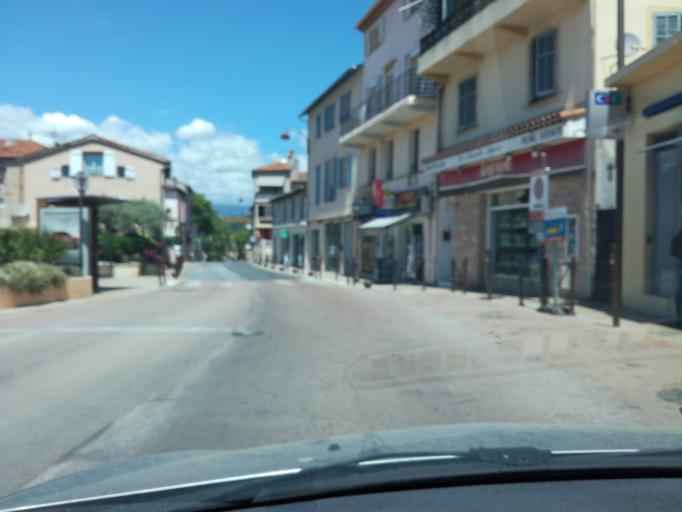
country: FR
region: Provence-Alpes-Cote d'Azur
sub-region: Departement des Alpes-Maritimes
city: Mougins
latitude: 43.5984
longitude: 6.9863
